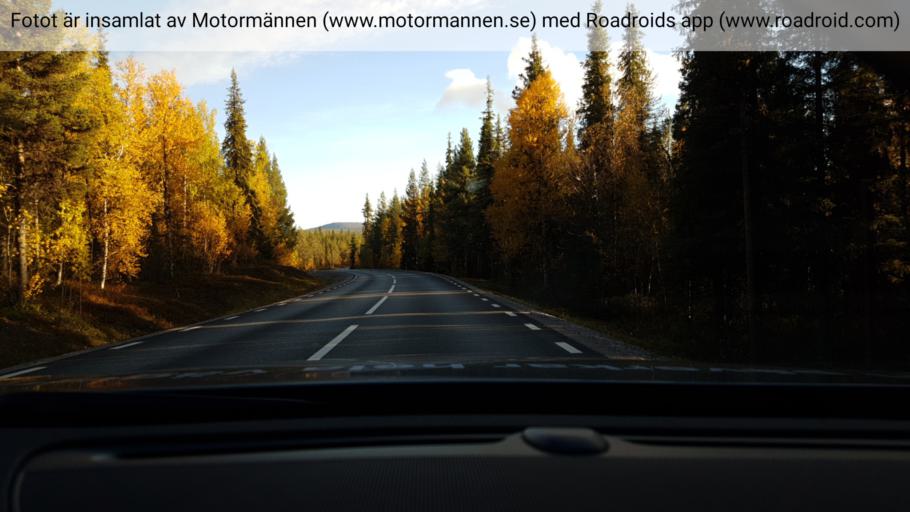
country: SE
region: Norrbotten
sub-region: Jokkmokks Kommun
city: Jokkmokk
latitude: 66.9325
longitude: 19.8205
